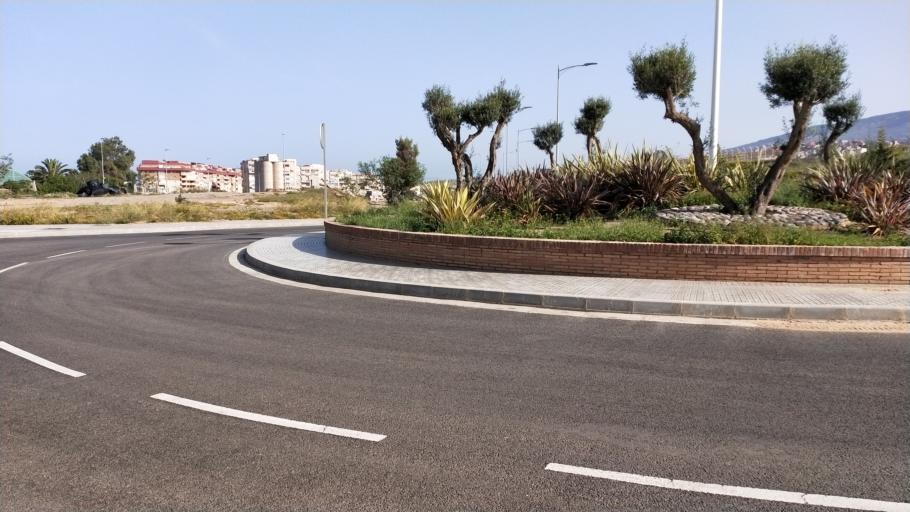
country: ES
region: Melilla
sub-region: Melilla
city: Melilla
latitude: 35.2771
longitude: -2.9520
